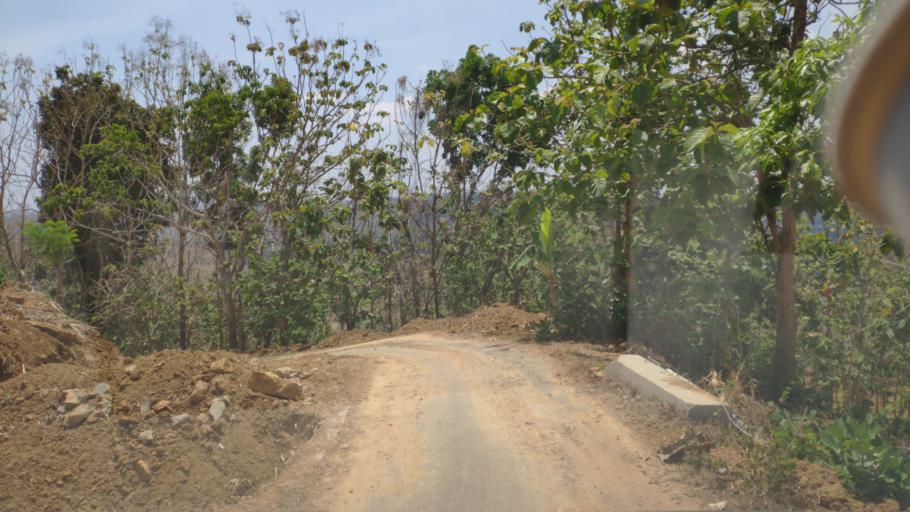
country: ID
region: Central Java
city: Guyangan
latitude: -6.9224
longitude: 111.1182
